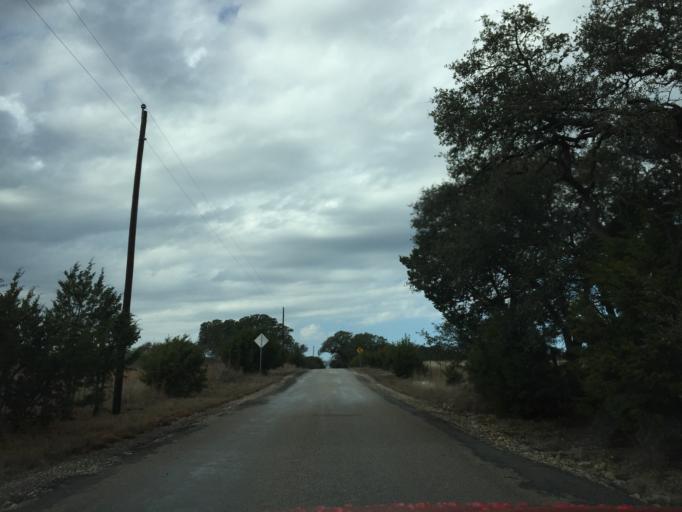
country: US
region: Texas
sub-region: Burnet County
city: Bertram
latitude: 30.6318
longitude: -98.0007
